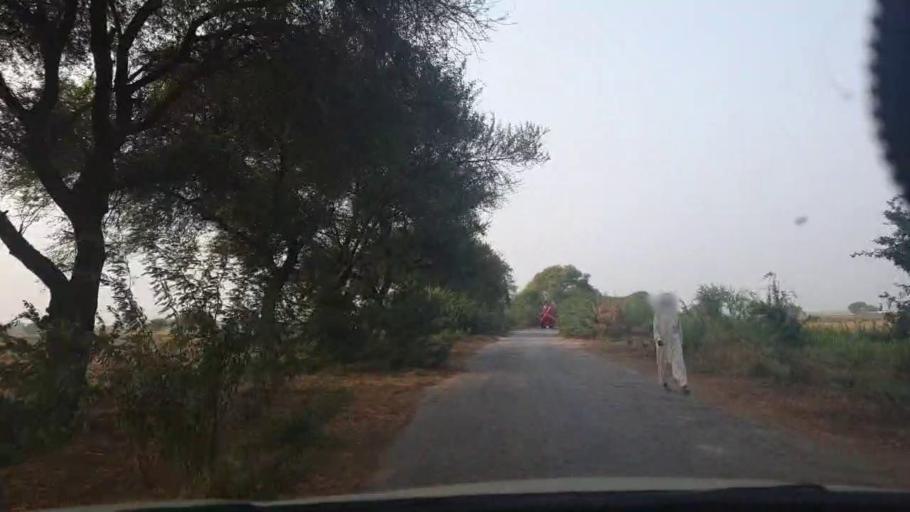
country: PK
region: Sindh
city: Bulri
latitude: 24.8080
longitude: 68.4094
